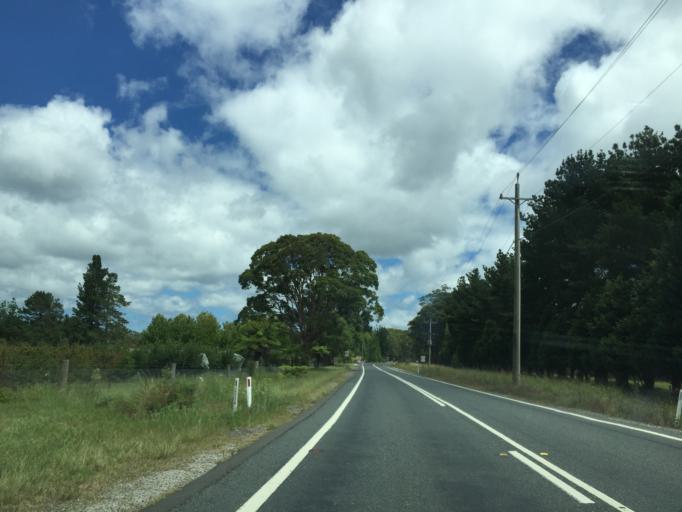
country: AU
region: New South Wales
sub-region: Hawkesbury
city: Richmond
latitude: -33.5142
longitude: 150.5777
